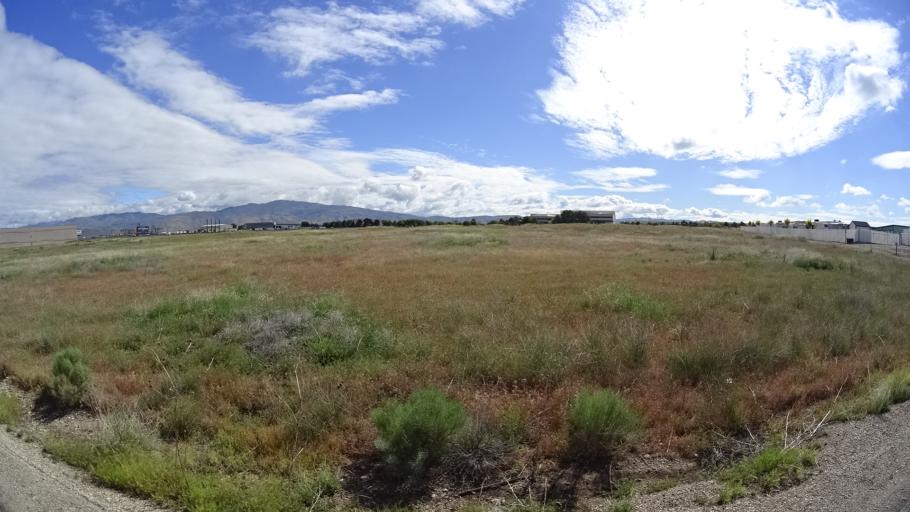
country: US
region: Idaho
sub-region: Ada County
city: Boise
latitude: 43.5293
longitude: -116.1567
